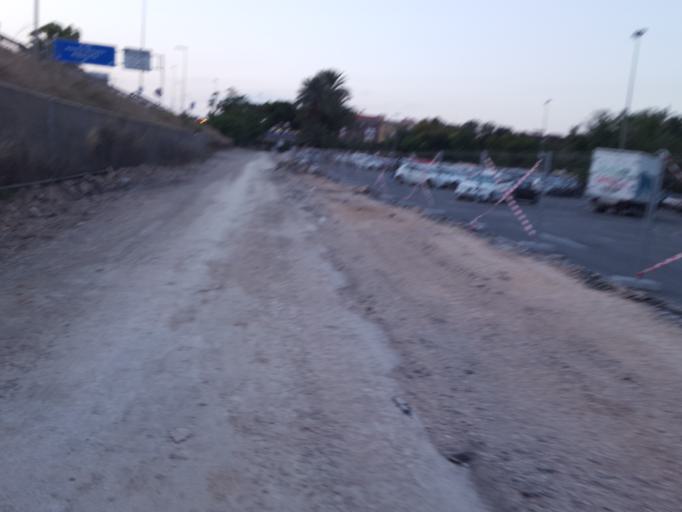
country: ES
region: Murcia
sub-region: Murcia
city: Murcia
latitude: 37.9801
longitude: -1.1375
